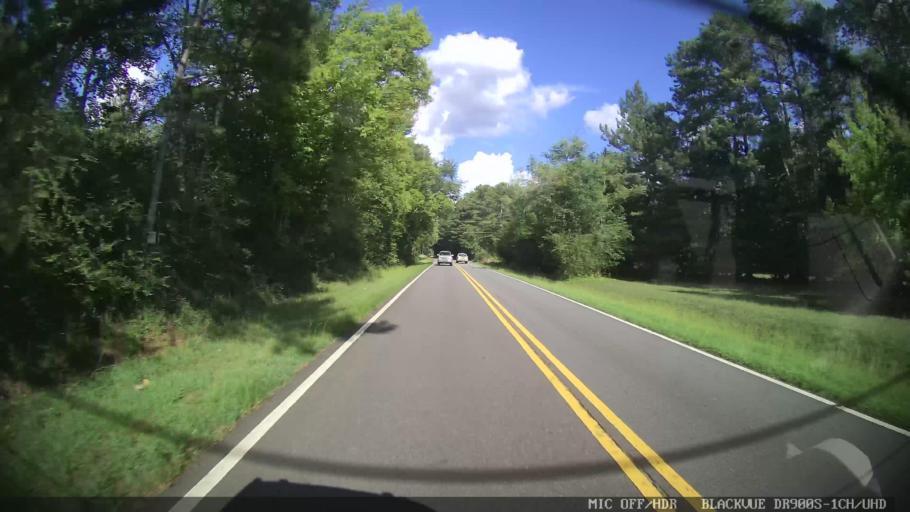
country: US
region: Georgia
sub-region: Bartow County
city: Euharlee
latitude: 34.1803
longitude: -85.0269
